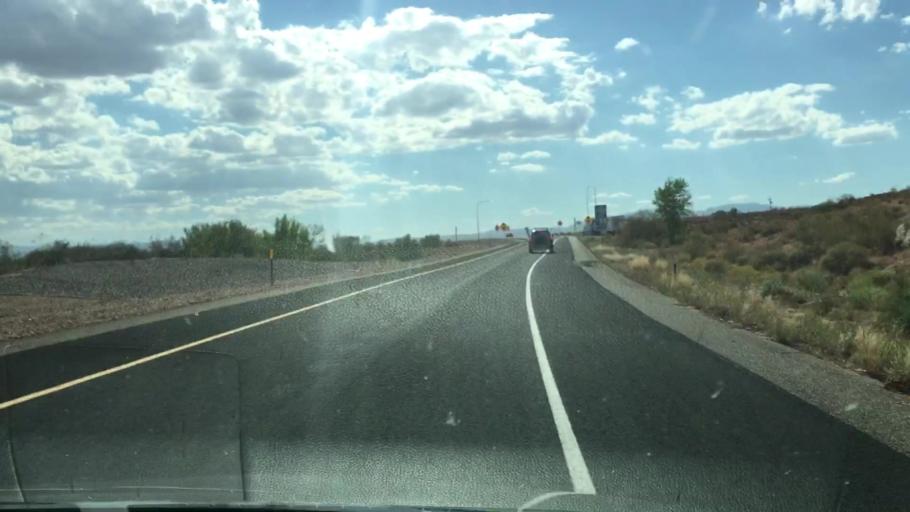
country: US
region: Utah
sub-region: Washington County
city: Washington
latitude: 37.1493
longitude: -113.4856
